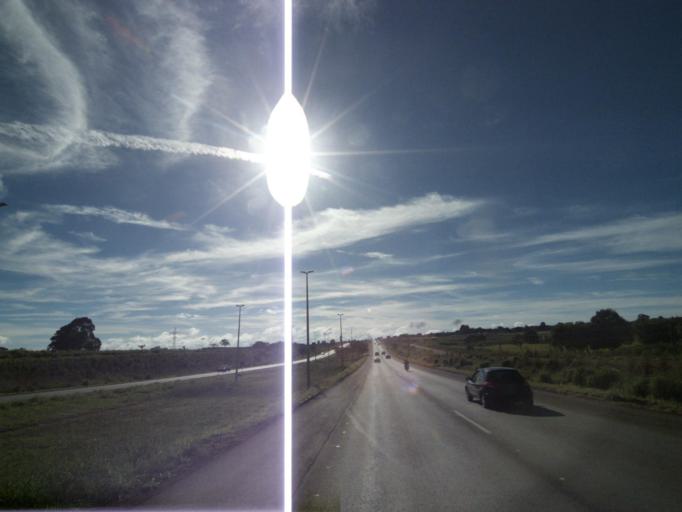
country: BR
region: Federal District
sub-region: Brasilia
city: Brasilia
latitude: -15.7904
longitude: -48.2145
